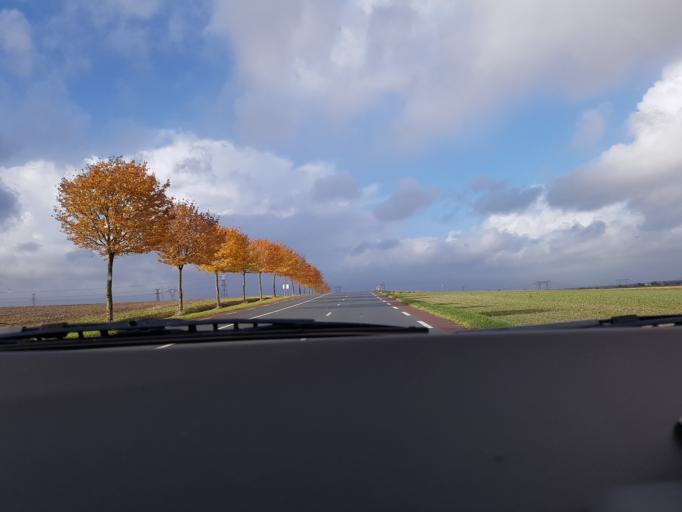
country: FR
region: Poitou-Charentes
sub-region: Departement de la Charente-Maritime
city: Les Gonds
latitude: 45.6633
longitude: -0.5949
